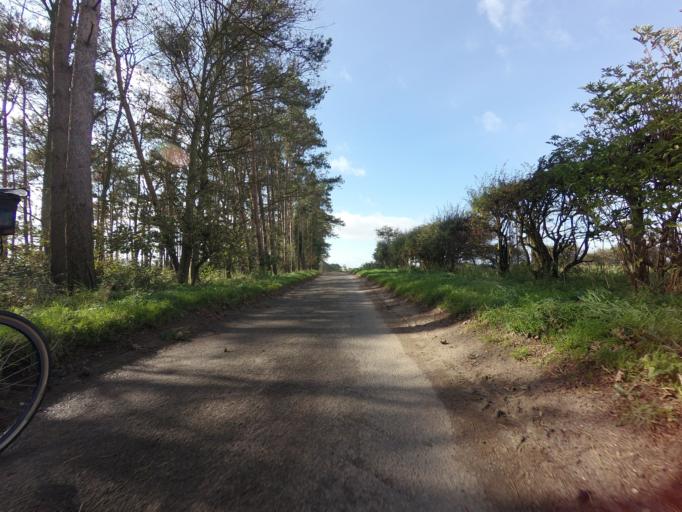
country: GB
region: England
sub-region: Norfolk
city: Hunstanton
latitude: 52.9366
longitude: 0.6327
